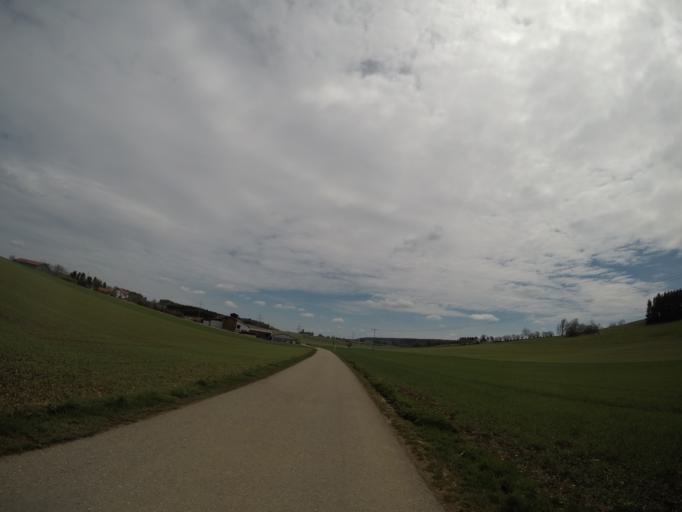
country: DE
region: Baden-Wuerttemberg
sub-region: Tuebingen Region
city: Westerheim
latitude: 48.5074
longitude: 9.6406
